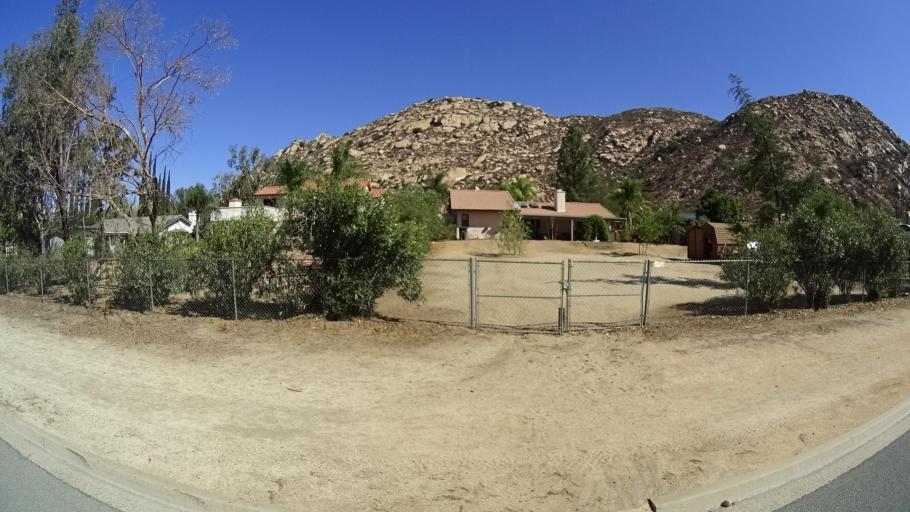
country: US
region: California
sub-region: San Diego County
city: San Diego Country Estates
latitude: 33.0058
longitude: -116.7813
